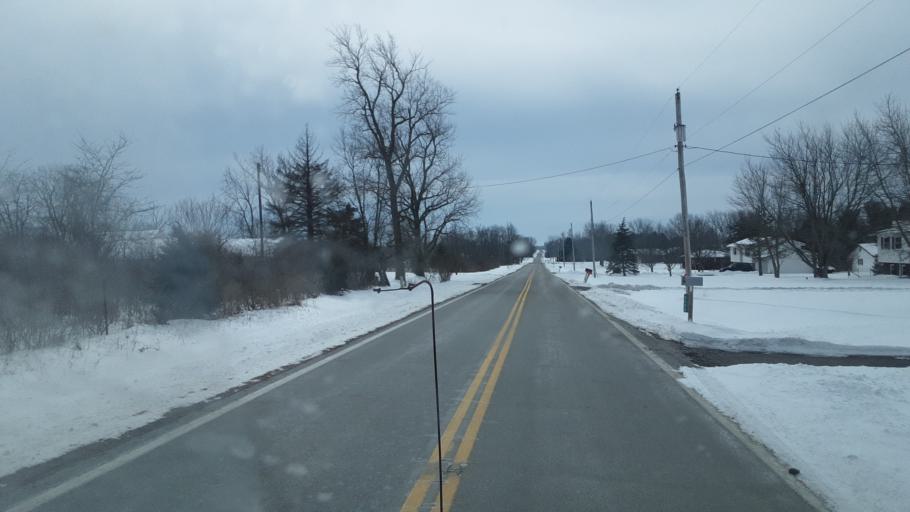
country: US
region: Ohio
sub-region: Madison County
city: Choctaw Lake
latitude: 39.9858
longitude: -83.4982
